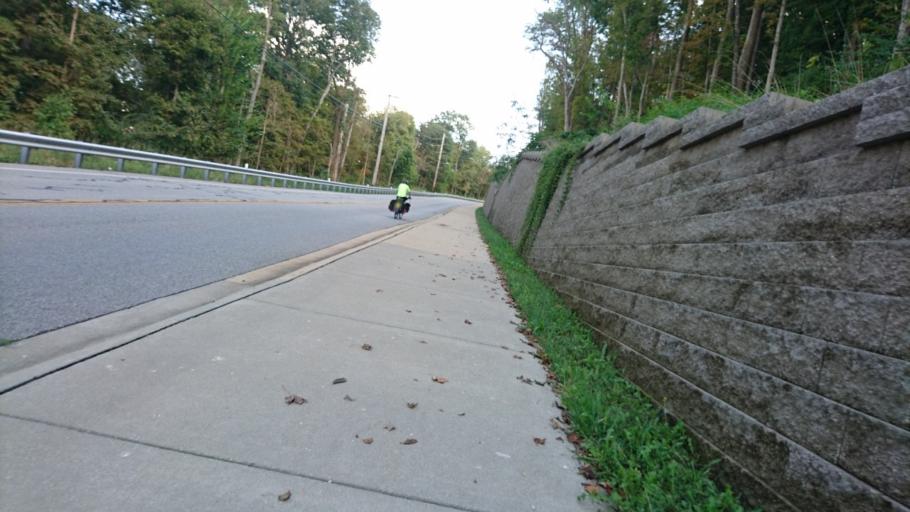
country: US
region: Missouri
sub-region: Saint Louis County
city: Eureka
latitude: 38.5146
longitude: -90.6339
